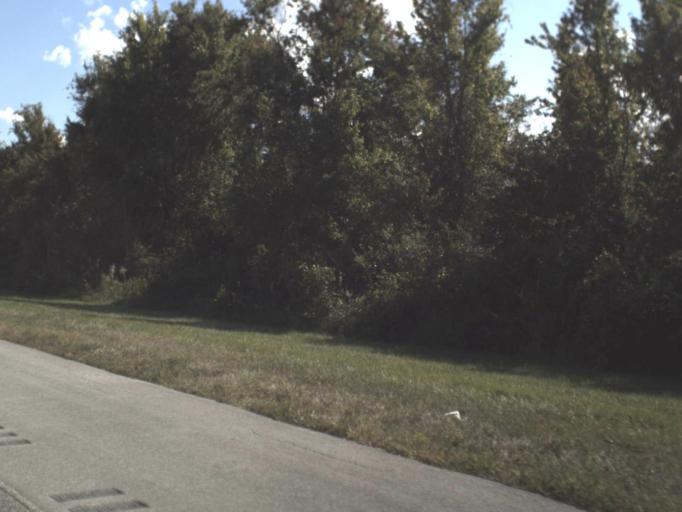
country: US
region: Florida
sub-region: Indian River County
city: Fellsmere
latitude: 27.7486
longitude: -80.9361
